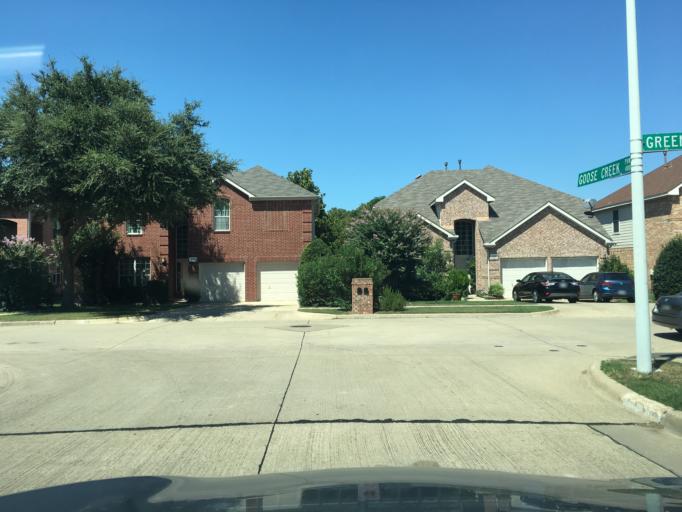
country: US
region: Texas
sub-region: Dallas County
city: Garland
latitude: 32.9526
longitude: -96.6425
